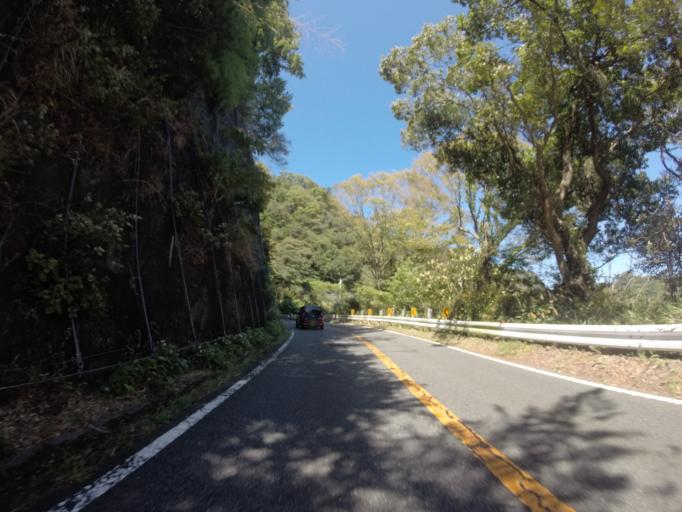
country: JP
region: Shizuoka
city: Yaizu
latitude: 34.8952
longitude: 138.3441
